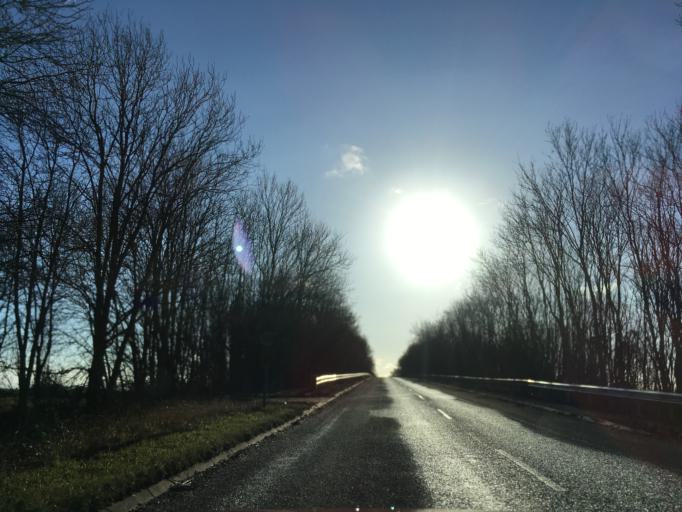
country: GB
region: England
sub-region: Wiltshire
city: Nettleton
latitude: 51.5210
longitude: -2.2748
